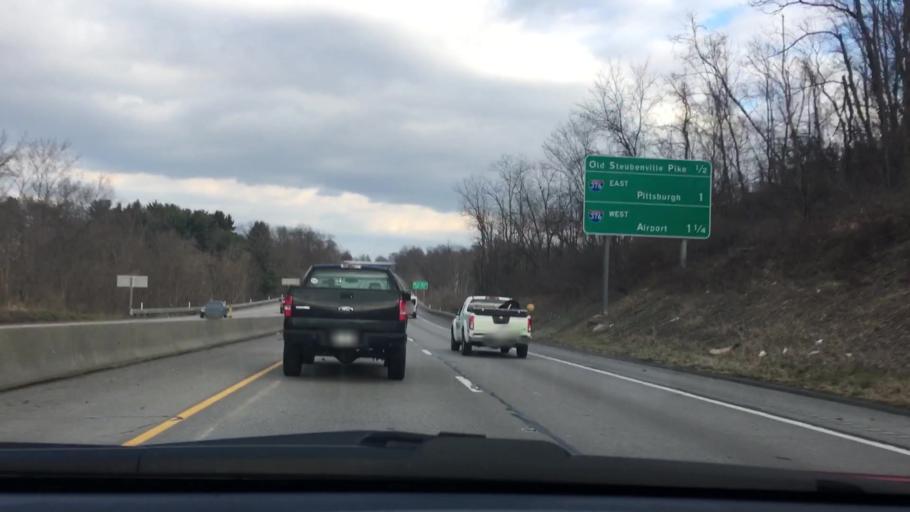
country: US
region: Pennsylvania
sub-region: Allegheny County
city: Oakdale
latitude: 40.4415
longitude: -80.1846
